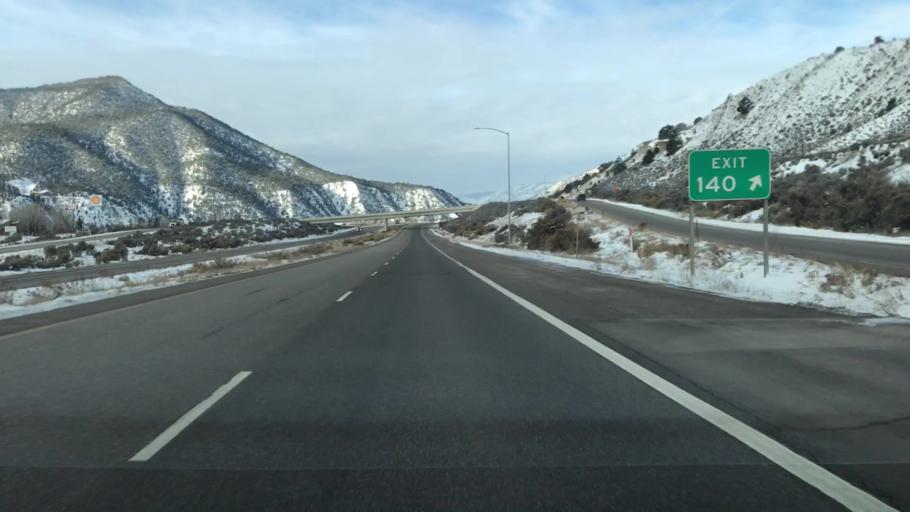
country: US
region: Colorado
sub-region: Eagle County
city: Gypsum
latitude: 39.6532
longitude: -106.9509
